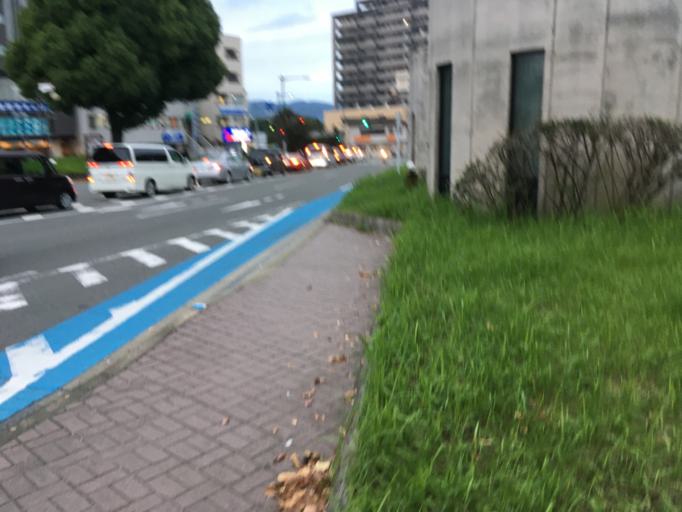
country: JP
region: Kumamoto
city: Kumamoto
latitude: 32.8054
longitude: 130.7258
